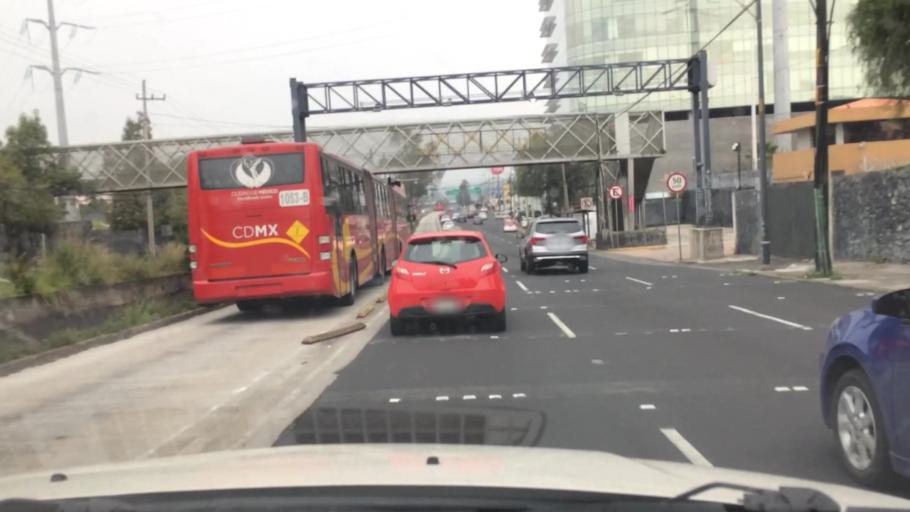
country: MX
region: Mexico City
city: Tlalpan
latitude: 19.3105
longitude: -99.1870
